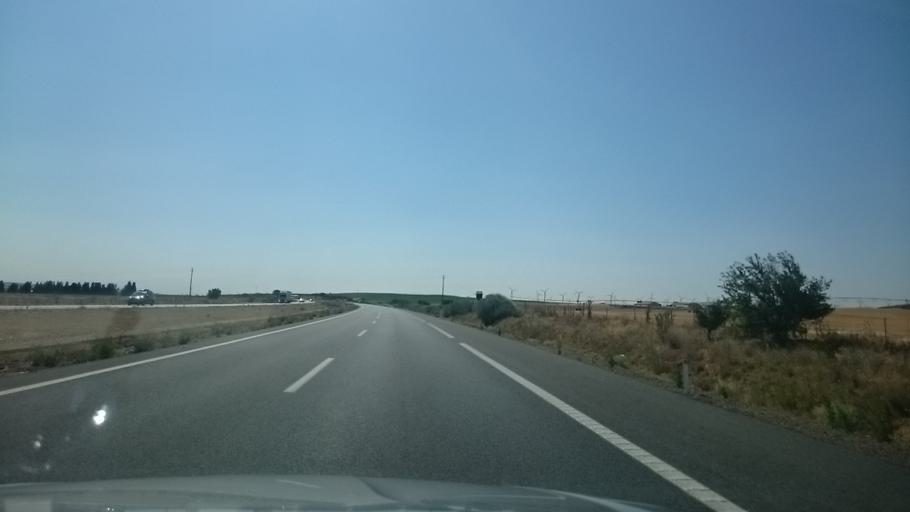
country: ES
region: Aragon
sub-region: Provincia de Zaragoza
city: Boquineni
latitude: 41.8216
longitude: -1.2895
